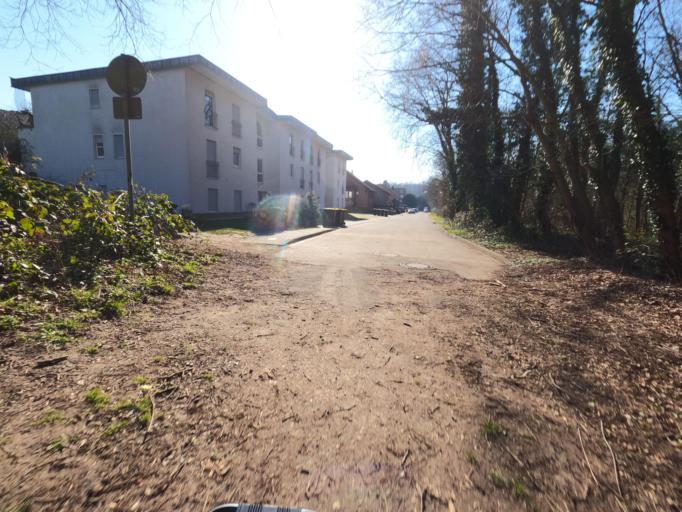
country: DE
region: North Rhine-Westphalia
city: Huckelhoven
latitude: 51.0641
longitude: 6.2216
